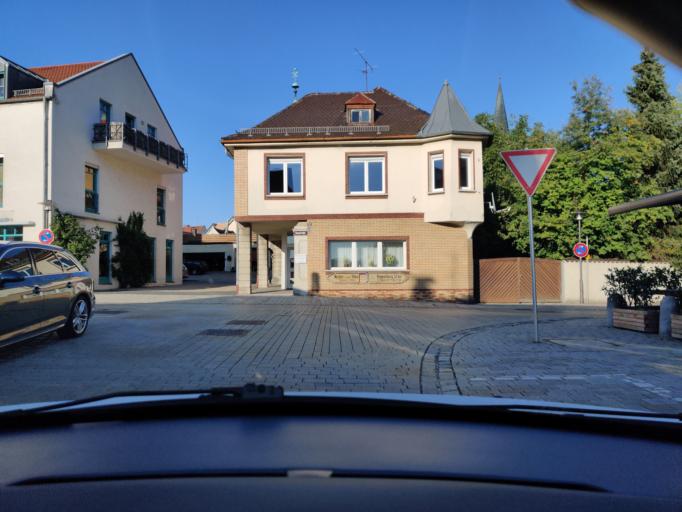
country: DE
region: Bavaria
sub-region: Upper Palatinate
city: Schwarzenfeld
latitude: 49.3889
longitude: 12.1390
